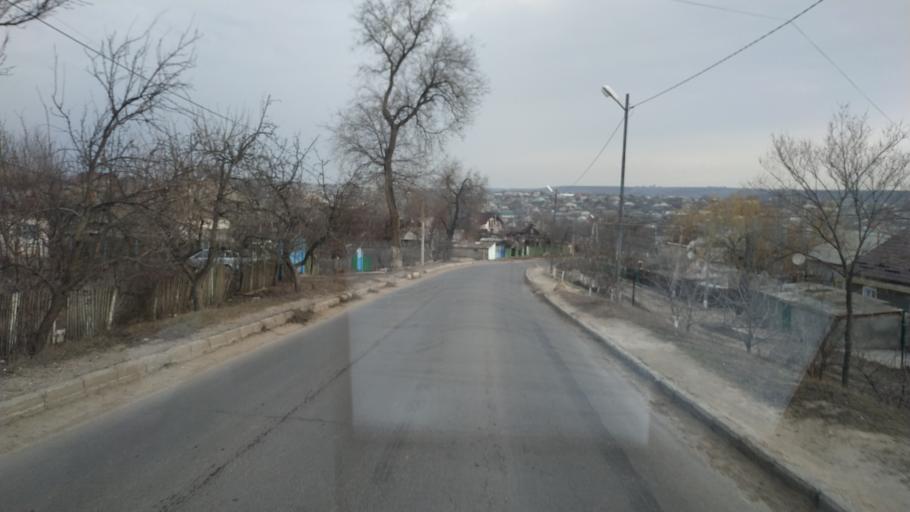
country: MD
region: Chisinau
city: Singera
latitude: 46.9555
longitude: 29.0582
